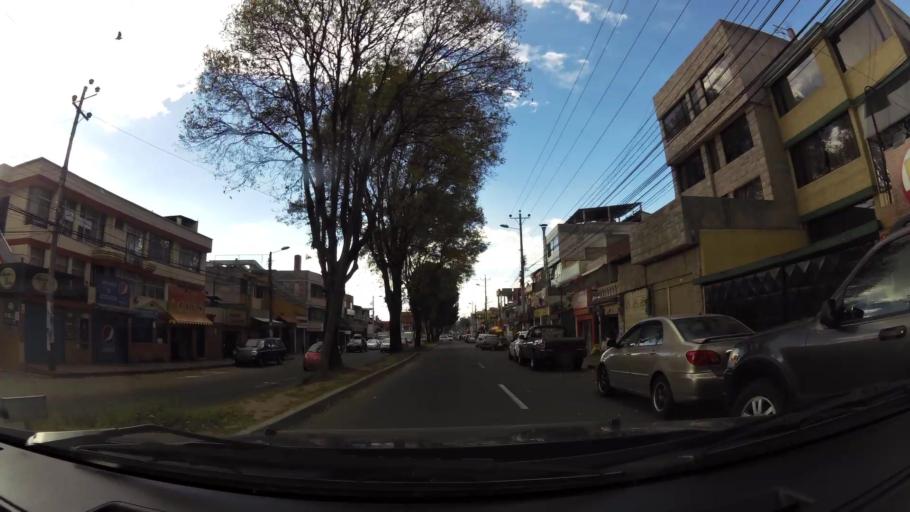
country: EC
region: Pichincha
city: Quito
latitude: -0.1253
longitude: -78.4862
